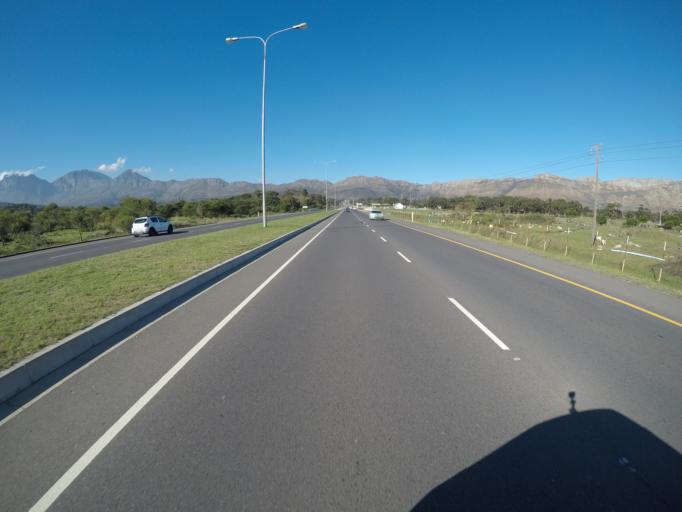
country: ZA
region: Western Cape
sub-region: Overberg District Municipality
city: Grabouw
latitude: -34.1237
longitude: 18.8880
